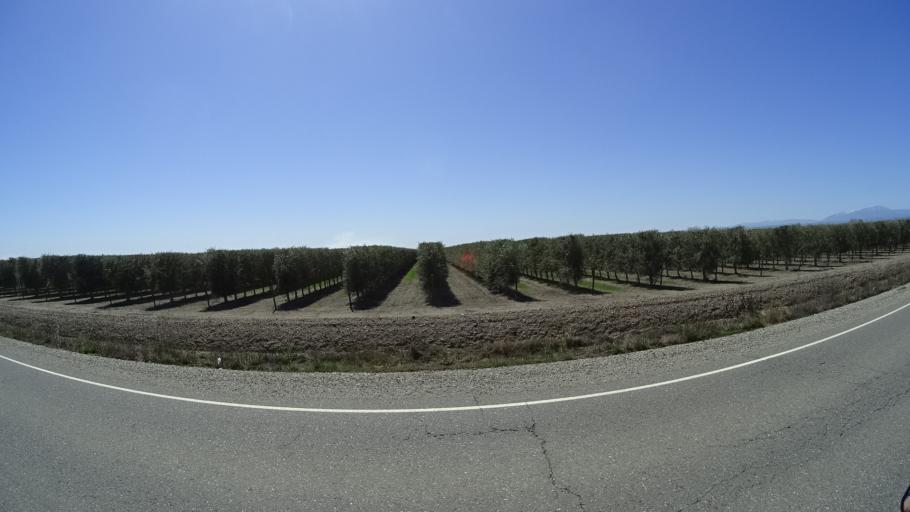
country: US
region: California
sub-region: Glenn County
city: Willows
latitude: 39.6247
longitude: -122.2447
